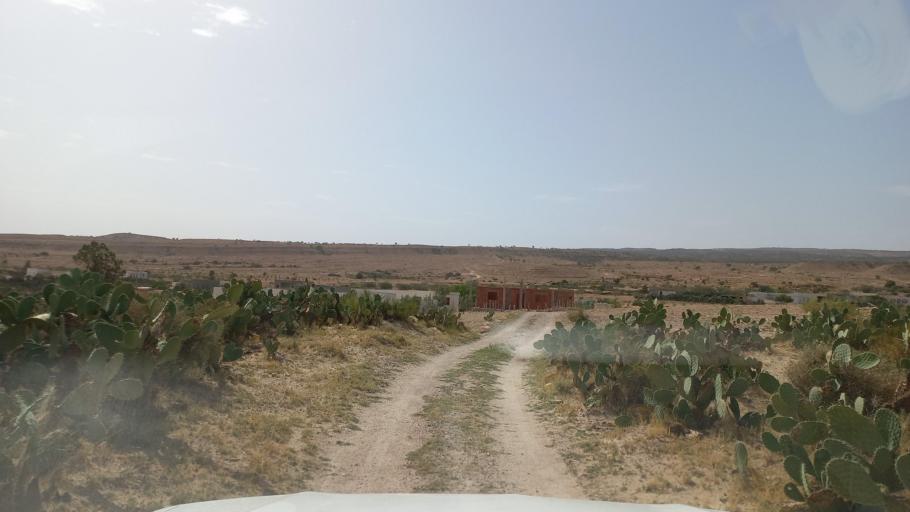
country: TN
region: Al Qasrayn
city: Kasserine
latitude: 35.3007
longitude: 8.9408
